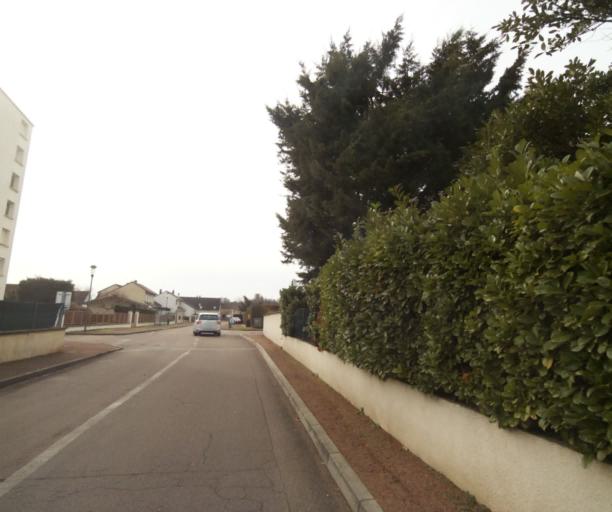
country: FR
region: Rhone-Alpes
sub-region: Departement de la Loire
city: Roanne
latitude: 46.0199
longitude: 4.0546
